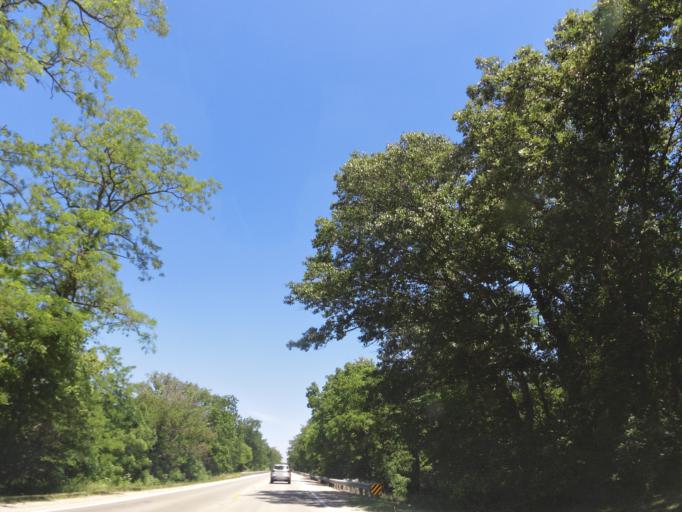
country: US
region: Illinois
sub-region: Iroquois County
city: Milford
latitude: 40.6033
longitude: -87.6949
